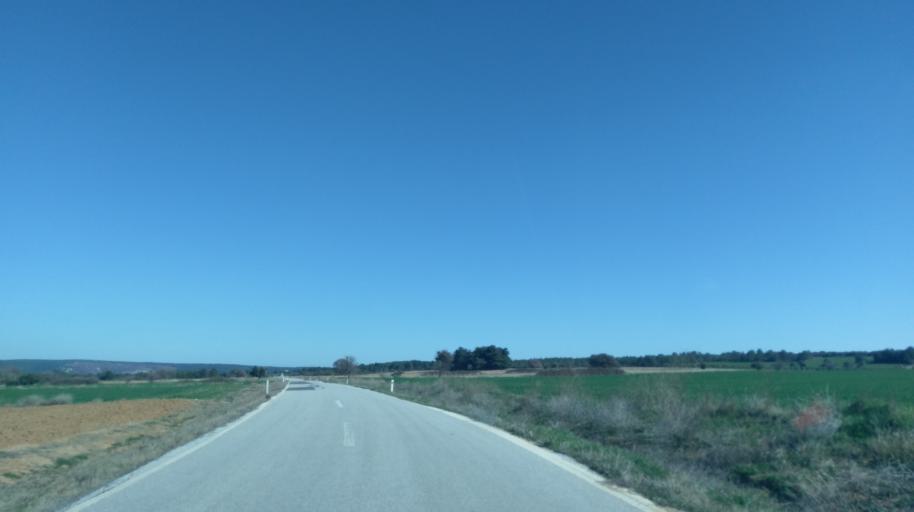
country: TR
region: Canakkale
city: Intepe
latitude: 40.1067
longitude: 26.2391
